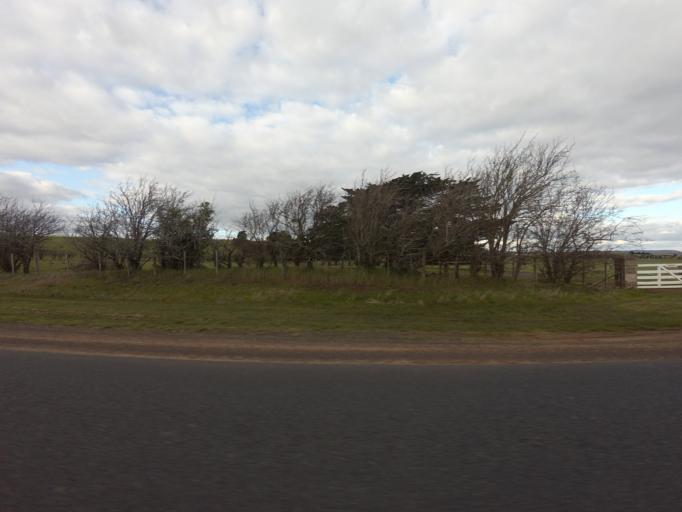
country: AU
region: Tasmania
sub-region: Northern Midlands
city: Evandale
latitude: -42.0186
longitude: 147.4919
